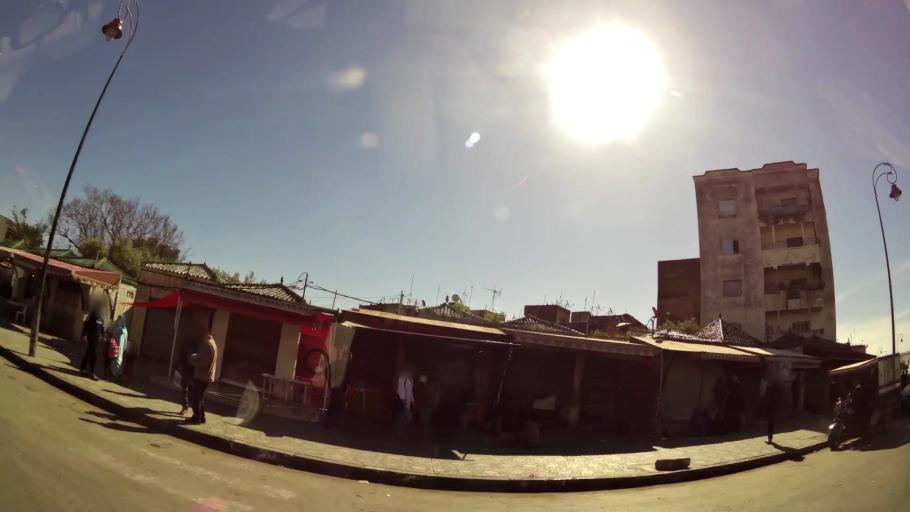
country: MA
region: Fes-Boulemane
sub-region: Fes
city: Fes
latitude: 34.0645
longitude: -4.9621
